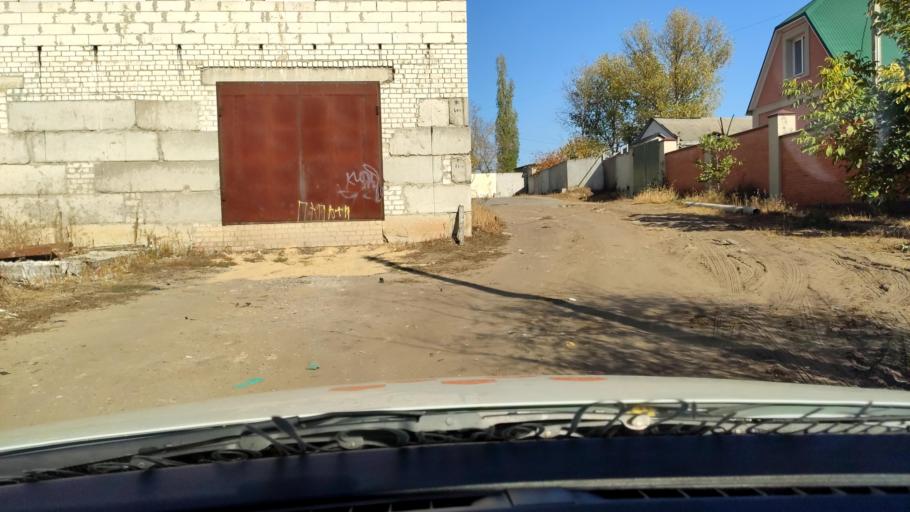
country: RU
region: Voronezj
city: Pridonskoy
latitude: 51.6854
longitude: 39.0649
